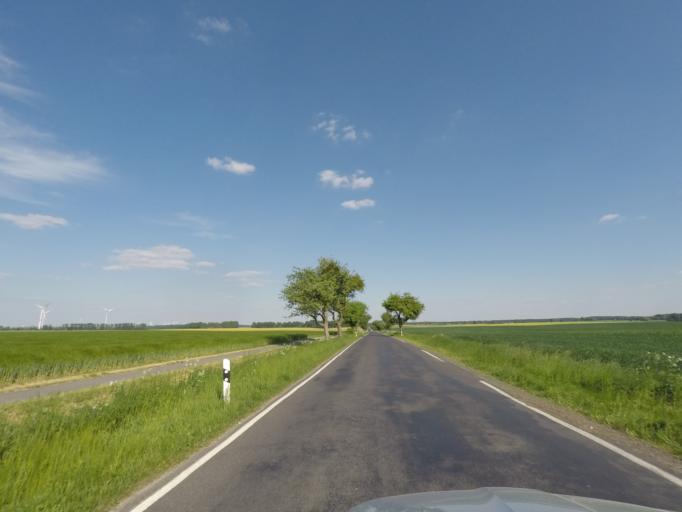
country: DE
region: Brandenburg
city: Werftpfuhl
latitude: 52.7358
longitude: 13.8438
